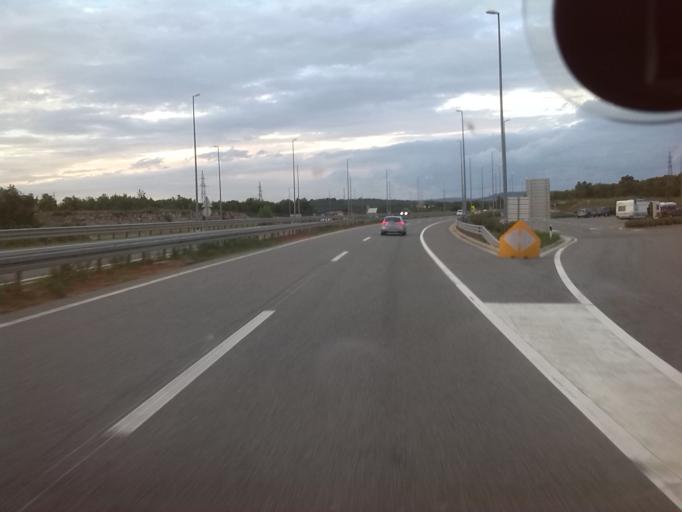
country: HR
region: Istarska
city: Buje
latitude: 45.4376
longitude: 13.6165
